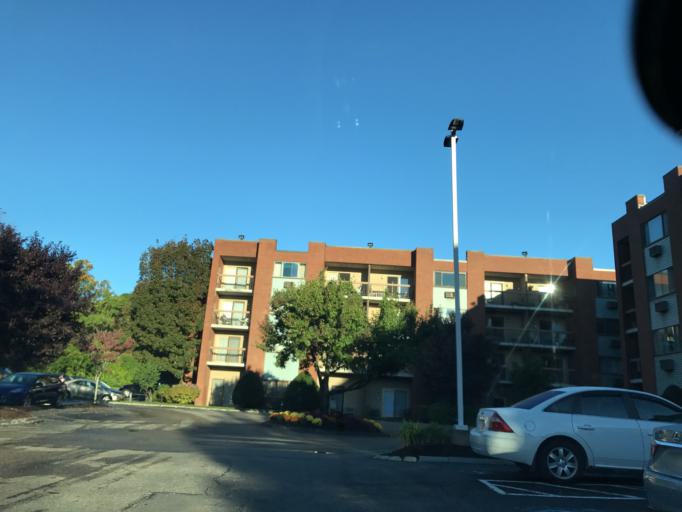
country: US
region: Massachusetts
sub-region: Norfolk County
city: Dedham
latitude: 42.2677
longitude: -71.1510
